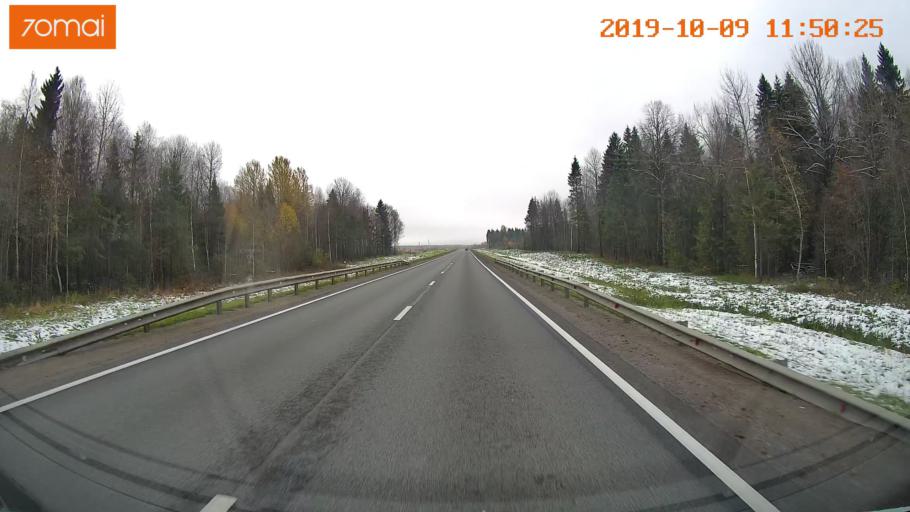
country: RU
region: Vologda
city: Gryazovets
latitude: 58.8057
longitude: 40.2462
